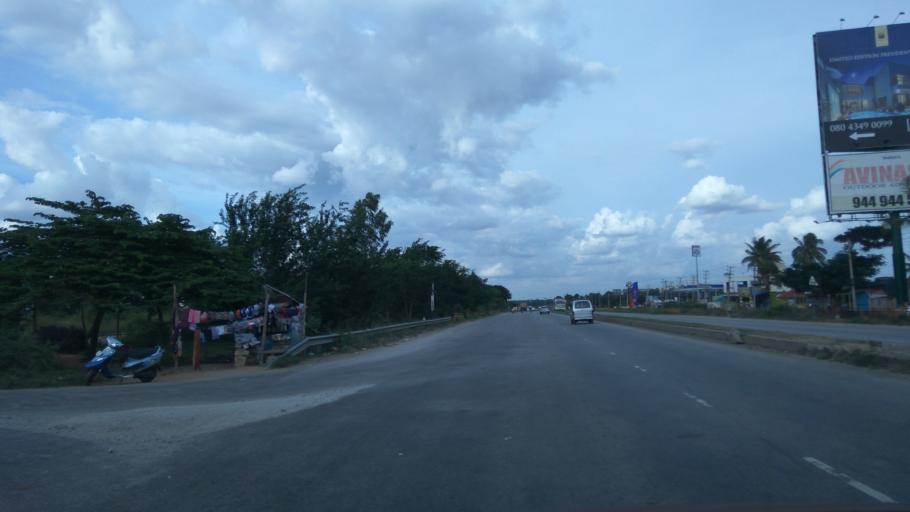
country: IN
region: Karnataka
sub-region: Bangalore Rural
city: Devanhalli
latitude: 13.2262
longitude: 77.6869
